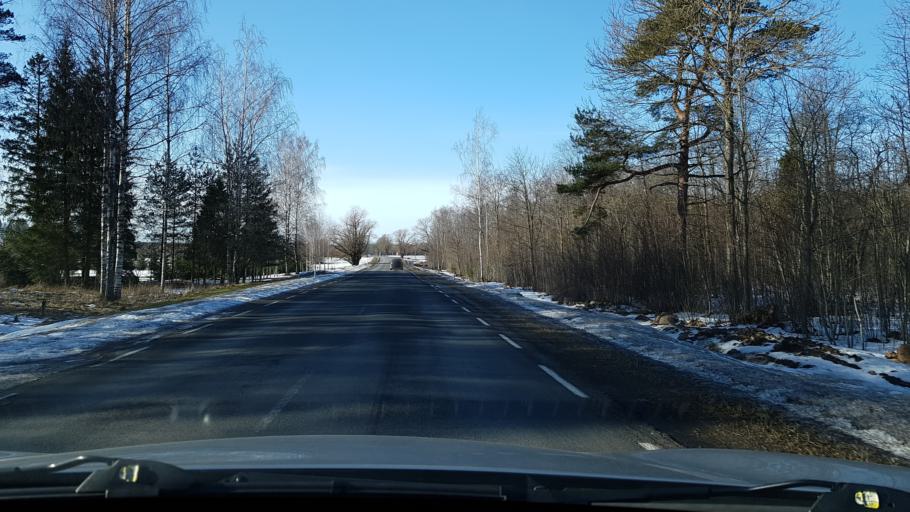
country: EE
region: Viljandimaa
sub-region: Vohma linn
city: Vohma
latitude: 58.6328
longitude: 25.5889
